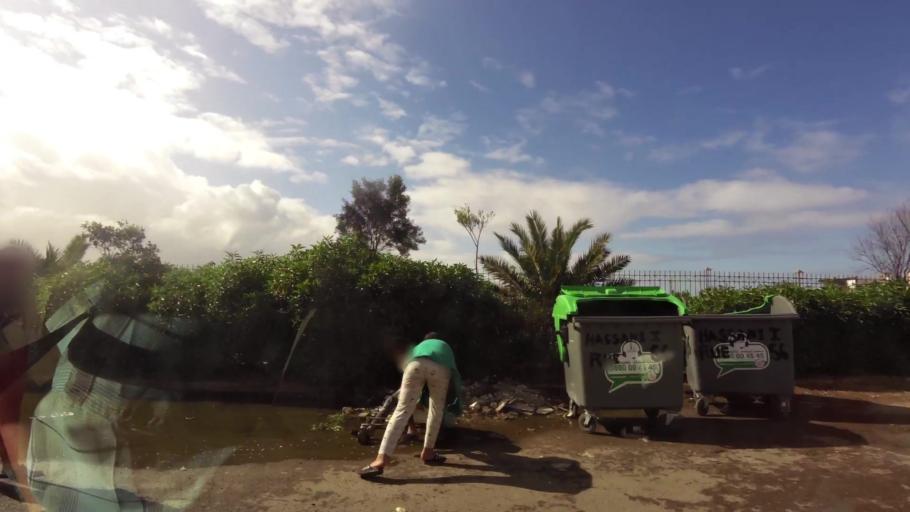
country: MA
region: Grand Casablanca
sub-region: Casablanca
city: Casablanca
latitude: 33.5678
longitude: -7.6968
